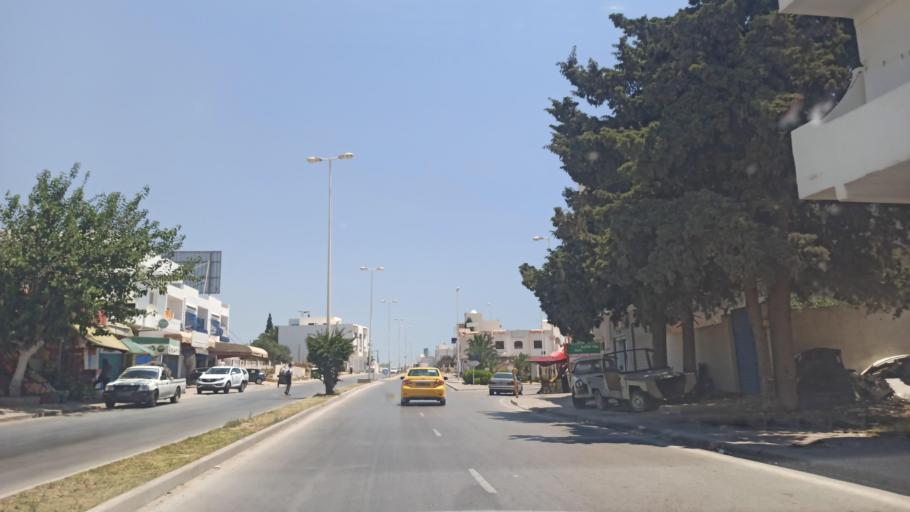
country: TN
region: Nabul
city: Al Hammamat
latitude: 36.4061
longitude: 10.6332
